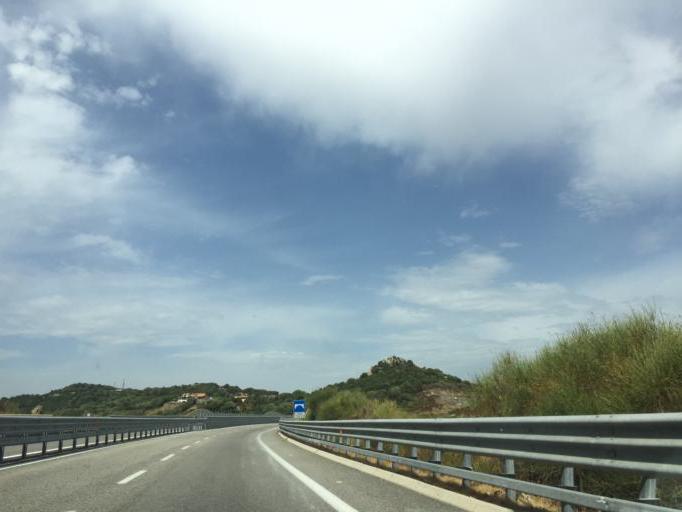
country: IT
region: Sardinia
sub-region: Provincia di Olbia-Tempio
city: San Teodoro
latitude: 40.7969
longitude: 9.6010
